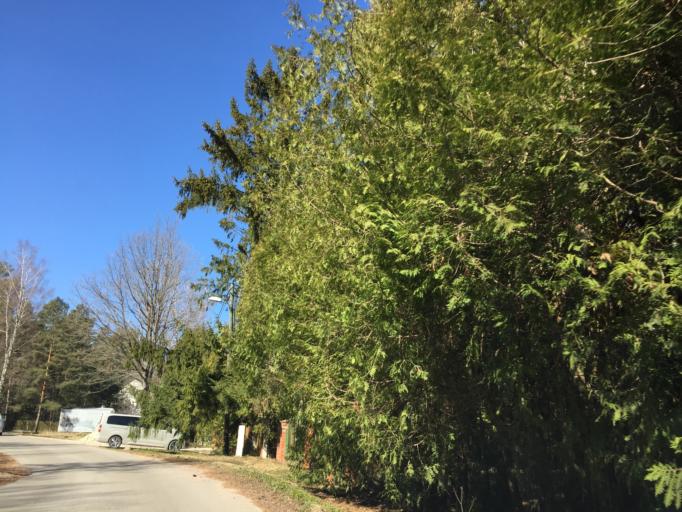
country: LV
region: Jurmala
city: Jurmala
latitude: 56.9413
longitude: 23.6867
